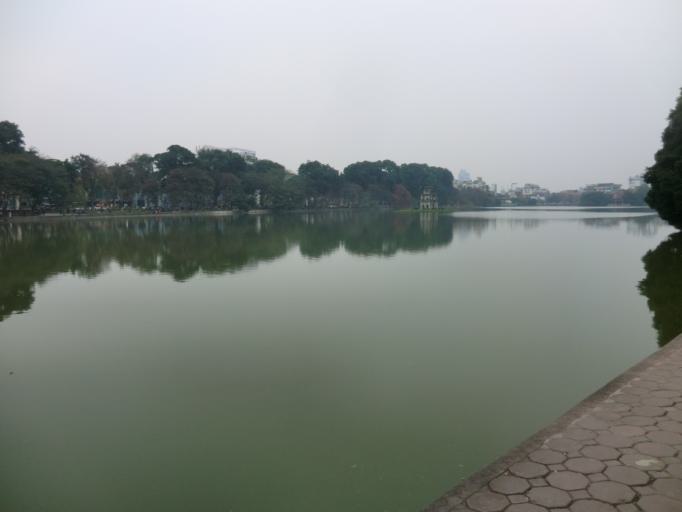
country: VN
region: Ha Noi
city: Hoan Kiem
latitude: 21.0263
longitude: 105.8532
